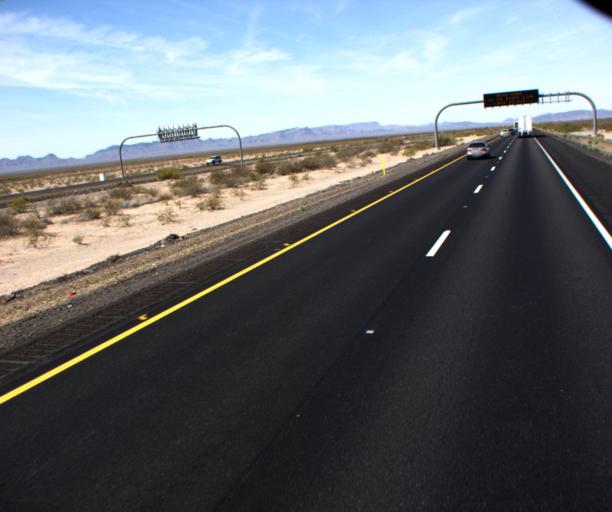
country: US
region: Arizona
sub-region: La Paz County
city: Salome
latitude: 33.6209
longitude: -113.6971
